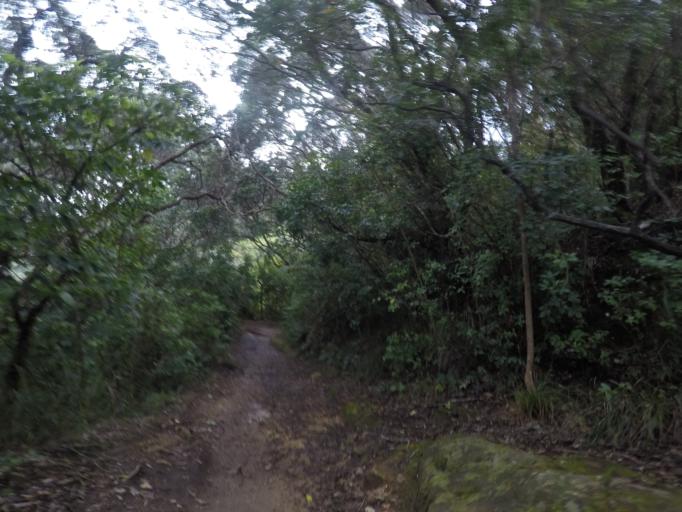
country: NZ
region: Bay of Plenty
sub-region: Western Bay of Plenty District
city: Waihi Beach
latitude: -37.3934
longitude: 175.9408
